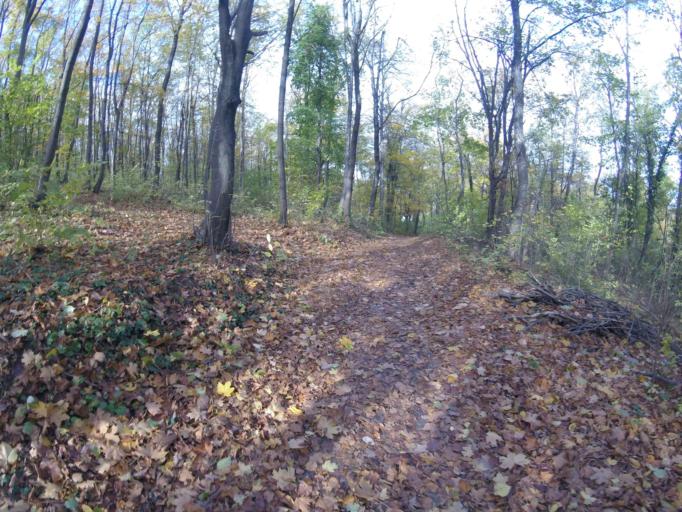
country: HU
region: Pest
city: Budakeszi
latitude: 47.5250
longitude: 18.9550
